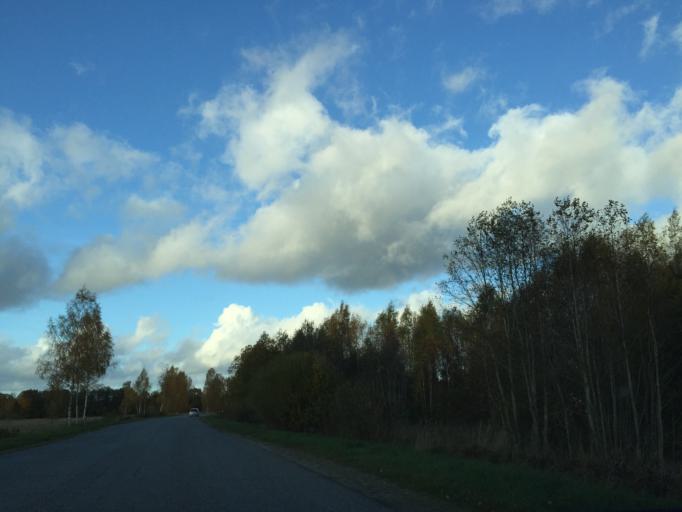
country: LV
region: Ogre
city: Jumprava
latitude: 56.7729
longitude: 25.0030
